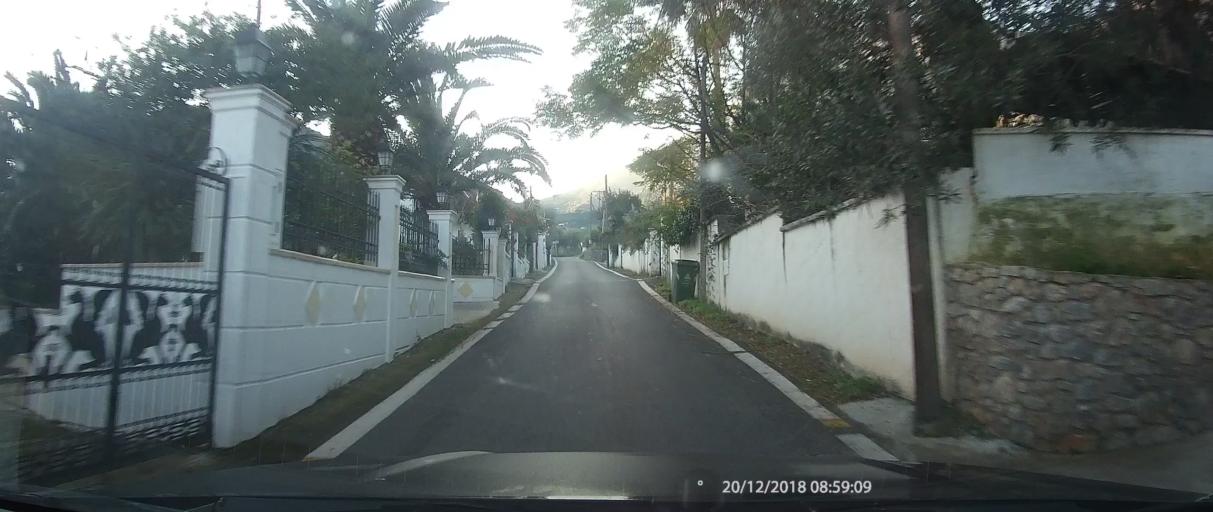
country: GR
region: Peloponnese
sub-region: Nomos Lakonias
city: Sykea
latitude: 36.9652
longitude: 22.9877
